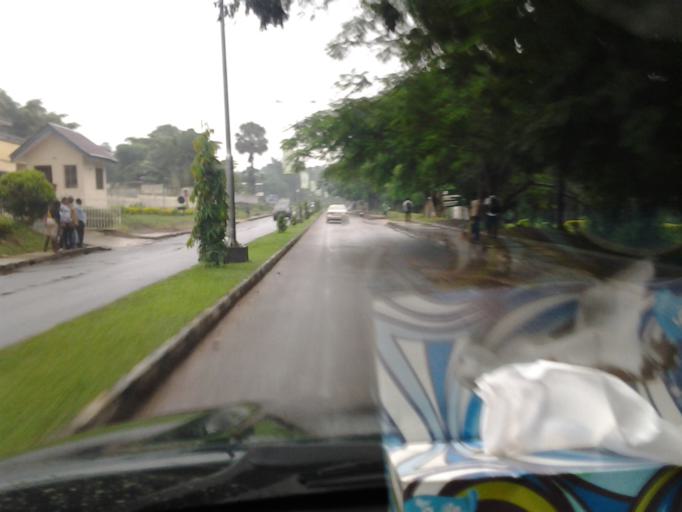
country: NG
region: Oyo
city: Ibadan
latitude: 7.4496
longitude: 3.8996
